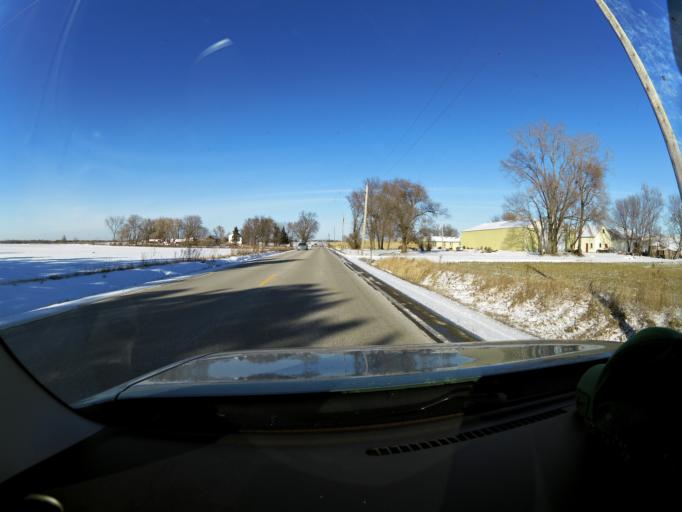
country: US
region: Minnesota
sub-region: Washington County
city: Cottage Grove
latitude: 44.8283
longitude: -92.8628
